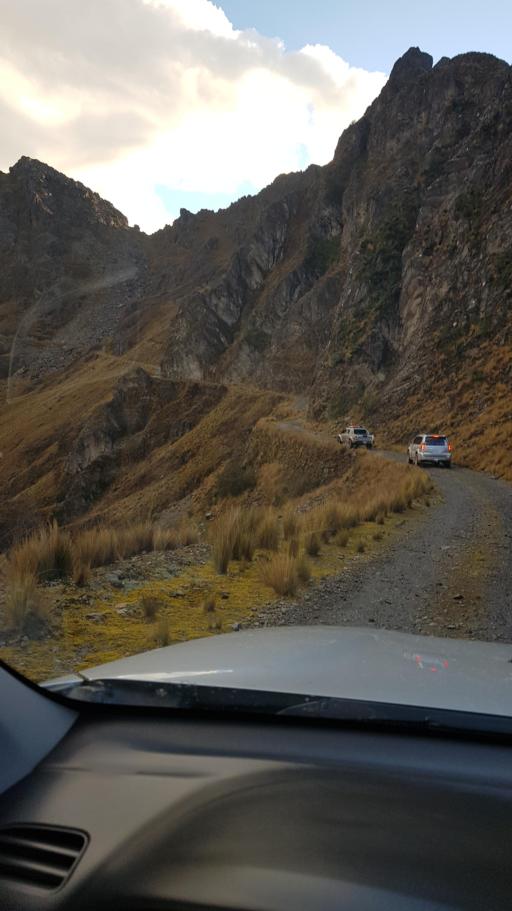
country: BO
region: Cochabamba
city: Colomi
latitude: -17.2706
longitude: -65.7333
